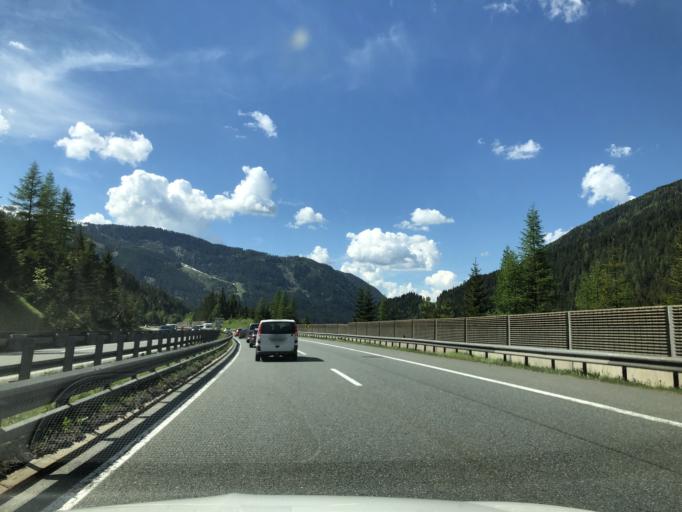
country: AT
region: Salzburg
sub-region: Politischer Bezirk Sankt Johann im Pongau
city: Flachau
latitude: 47.2797
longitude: 13.4105
